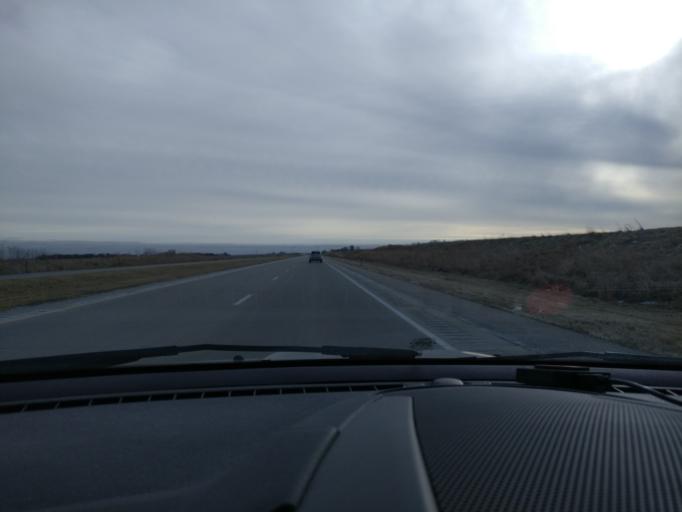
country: US
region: Nebraska
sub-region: Saunders County
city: Wahoo
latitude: 41.1540
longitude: -96.6312
